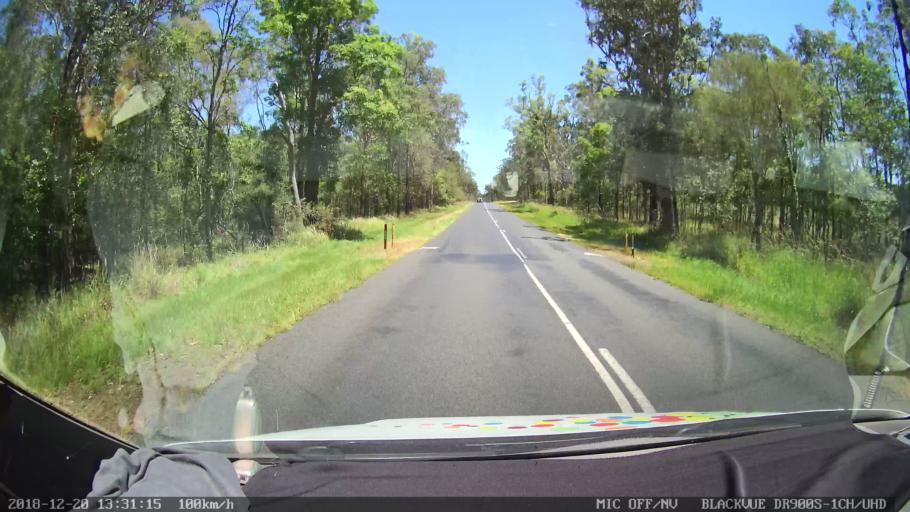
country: AU
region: New South Wales
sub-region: Clarence Valley
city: Gordon
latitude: -29.2153
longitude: 152.9897
